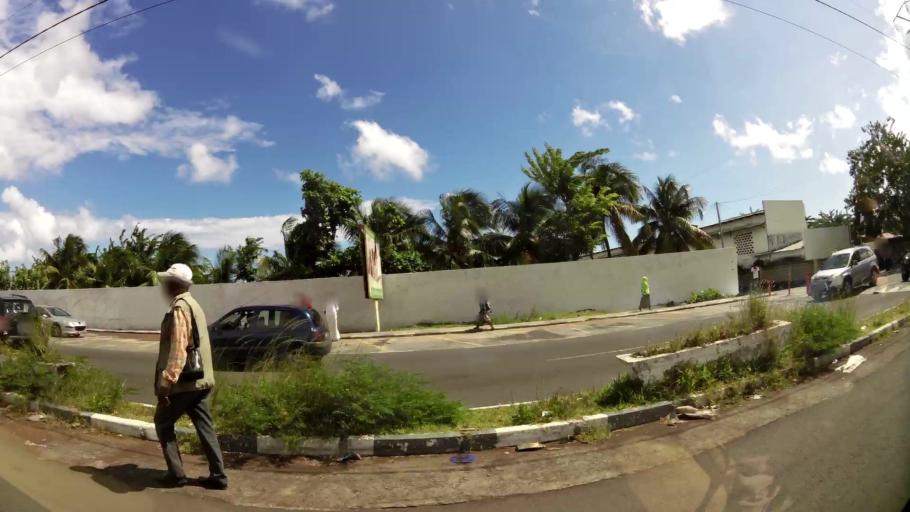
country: KM
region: Grande Comore
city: Mavingouni
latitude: -11.7160
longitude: 43.2457
